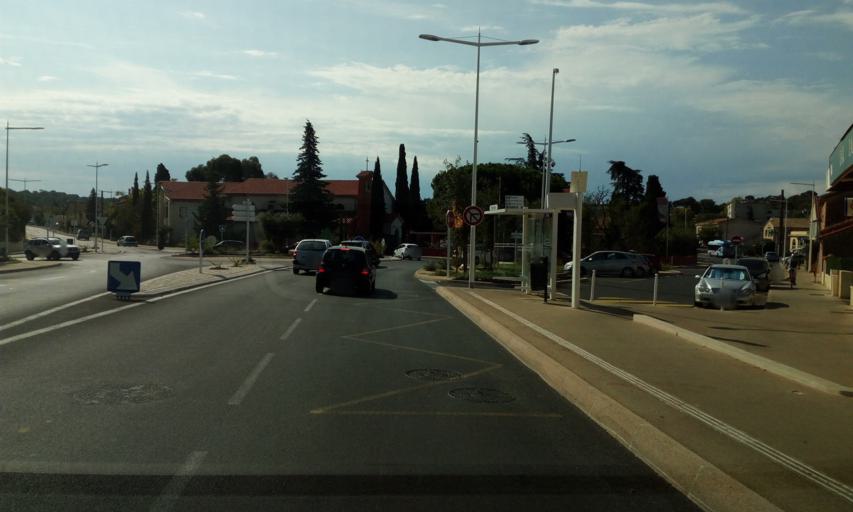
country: FR
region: Provence-Alpes-Cote d'Azur
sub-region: Departement du Var
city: La Valette-du-Var
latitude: 43.1178
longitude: 5.9811
